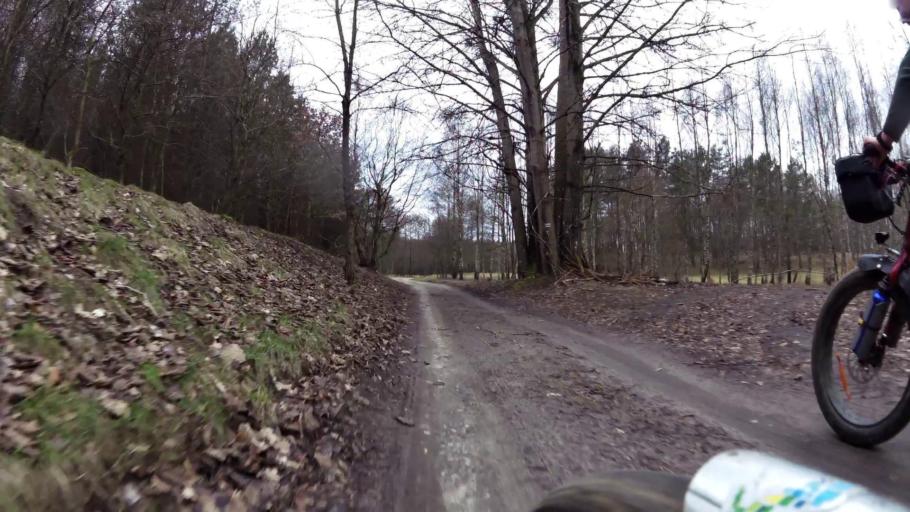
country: PL
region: Pomeranian Voivodeship
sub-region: Powiat bytowski
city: Trzebielino
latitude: 54.1177
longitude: 17.1284
